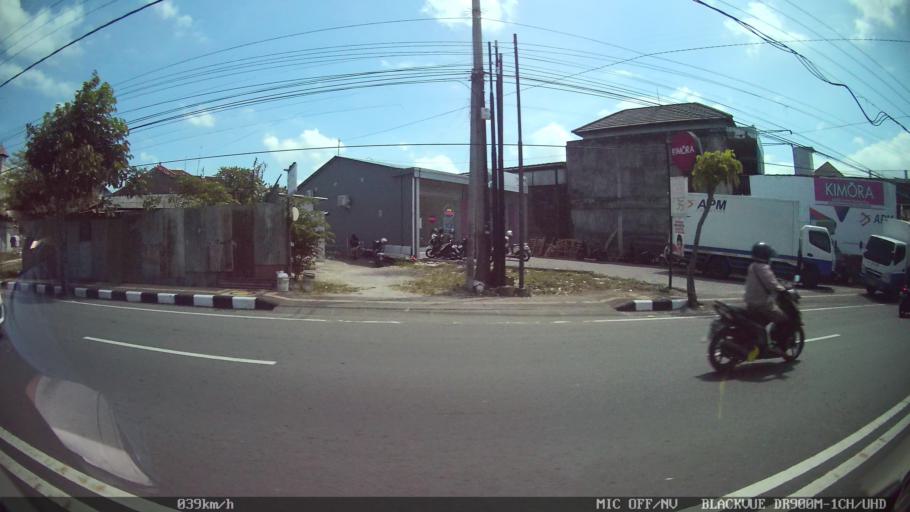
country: ID
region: Bali
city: Denpasar
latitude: -8.6561
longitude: 115.1919
